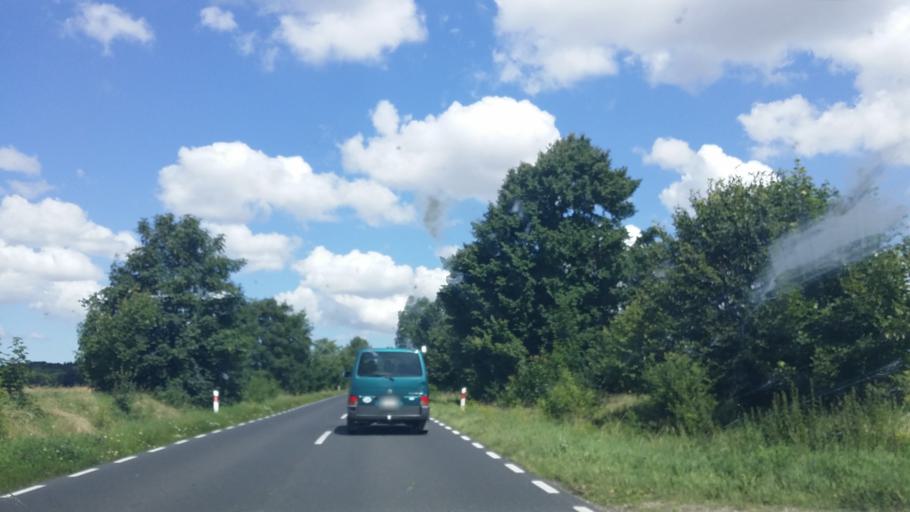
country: PL
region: West Pomeranian Voivodeship
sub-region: Powiat kolobrzeski
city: Goscino
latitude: 53.9927
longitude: 15.6744
